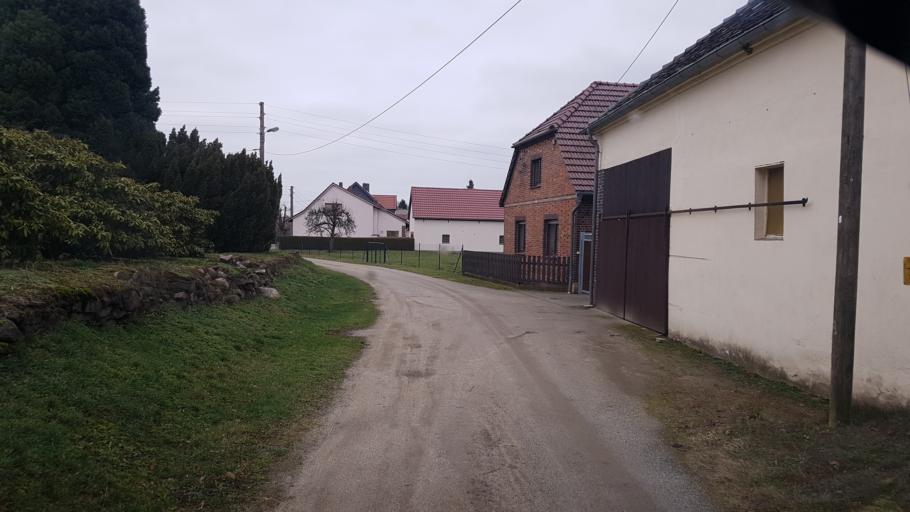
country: DE
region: Brandenburg
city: Crinitz
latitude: 51.7382
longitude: 13.7252
